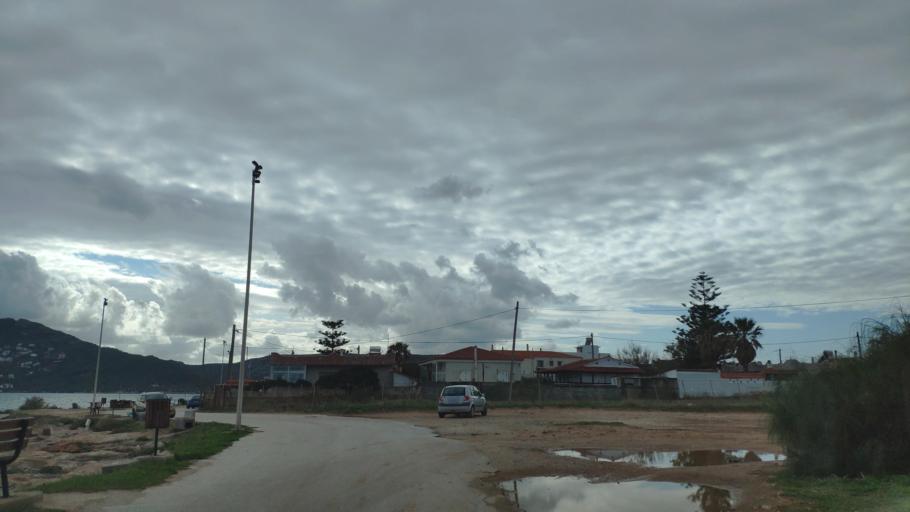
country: GR
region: Attica
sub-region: Nomarchia Anatolikis Attikis
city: Artemida
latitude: 37.9400
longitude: 24.0164
